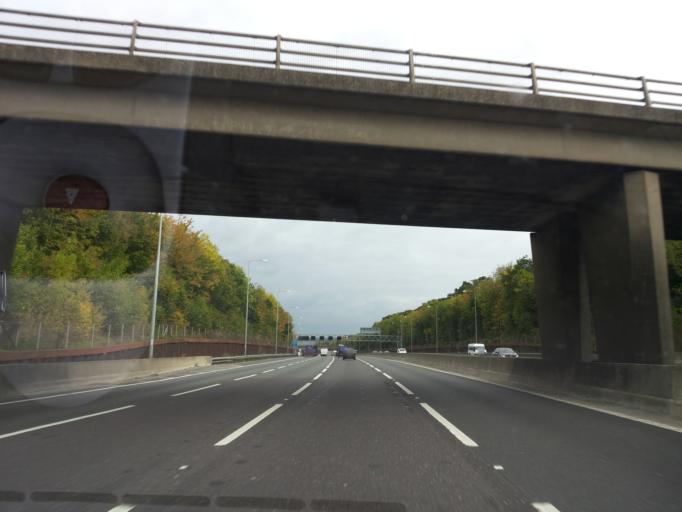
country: GB
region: England
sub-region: Hertfordshire
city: St Albans
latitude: 51.7120
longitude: -0.3612
